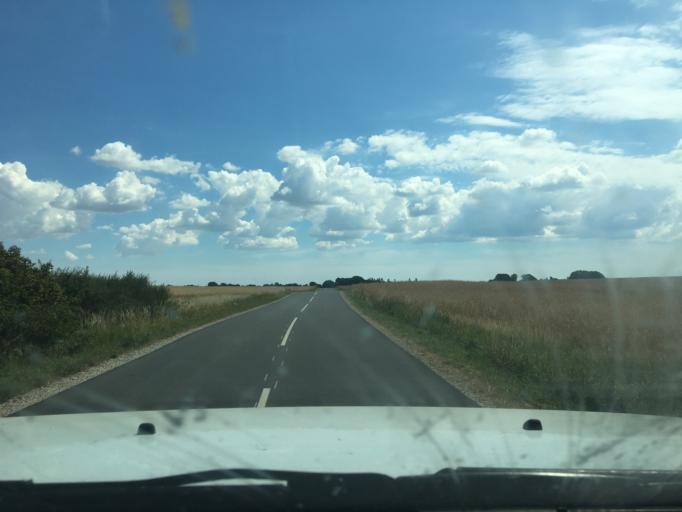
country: DK
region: Central Jutland
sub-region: Syddjurs Kommune
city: Hornslet
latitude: 56.3498
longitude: 10.2466
